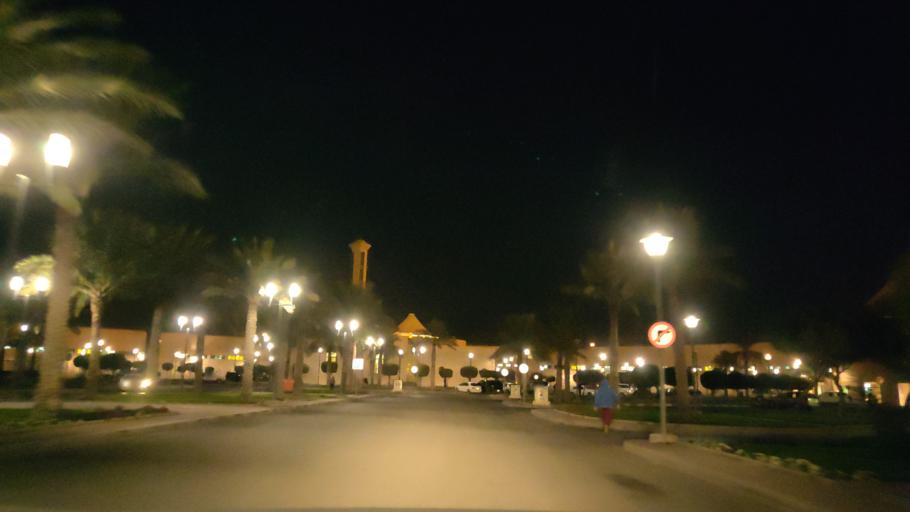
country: KW
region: Al Asimah
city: Ar Rabiyah
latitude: 29.2529
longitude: 47.8441
